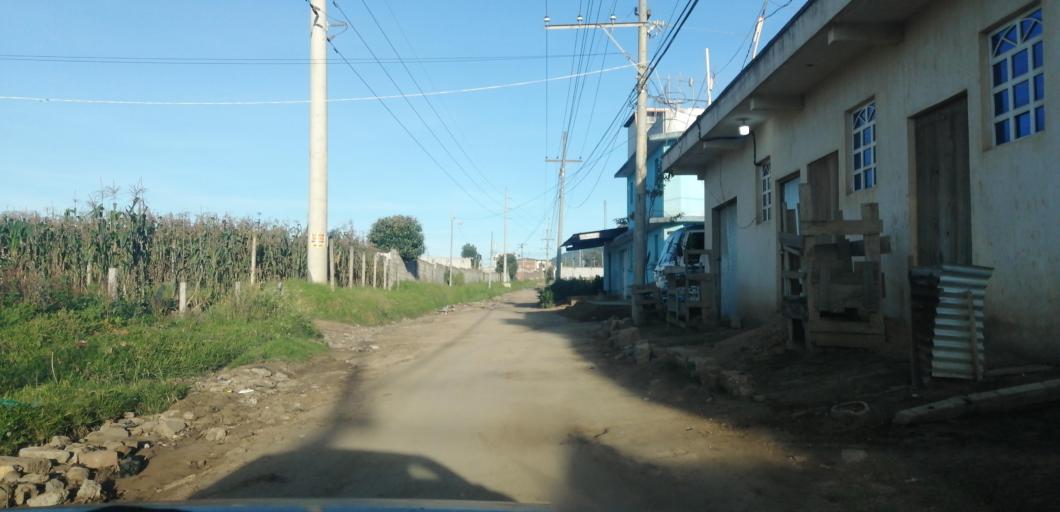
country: GT
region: Quetzaltenango
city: Olintepeque
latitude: 14.8683
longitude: -91.5307
